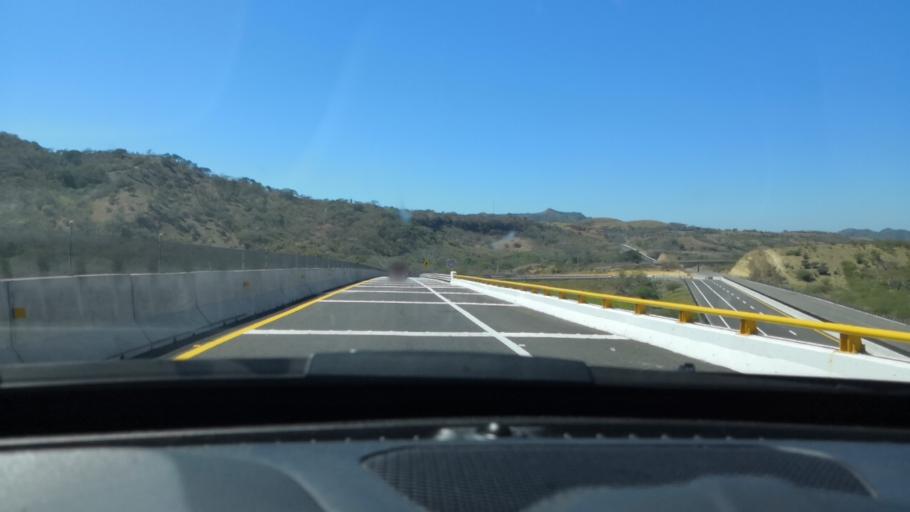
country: MX
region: Nayarit
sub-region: Compostela
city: Juan Escutia (Borbollon)
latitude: 21.1385
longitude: -104.9214
